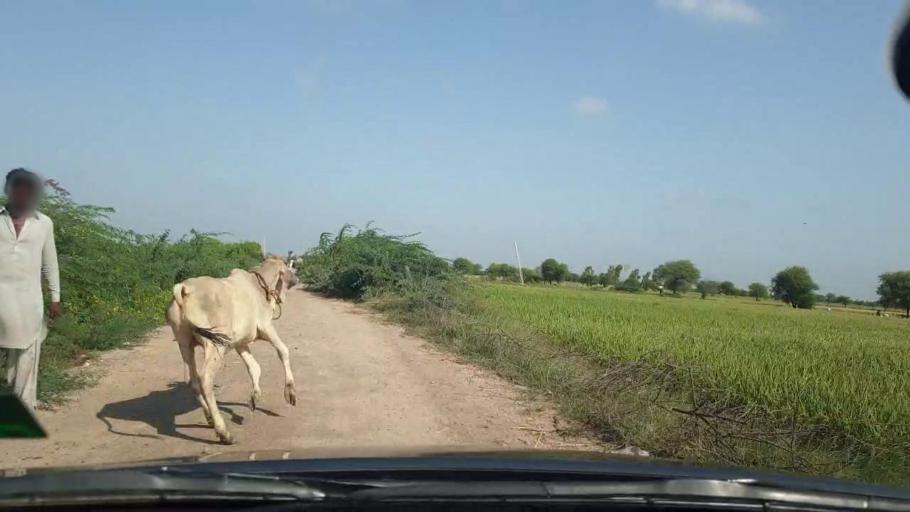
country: PK
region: Sindh
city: Tando Bago
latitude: 24.7438
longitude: 68.9810
